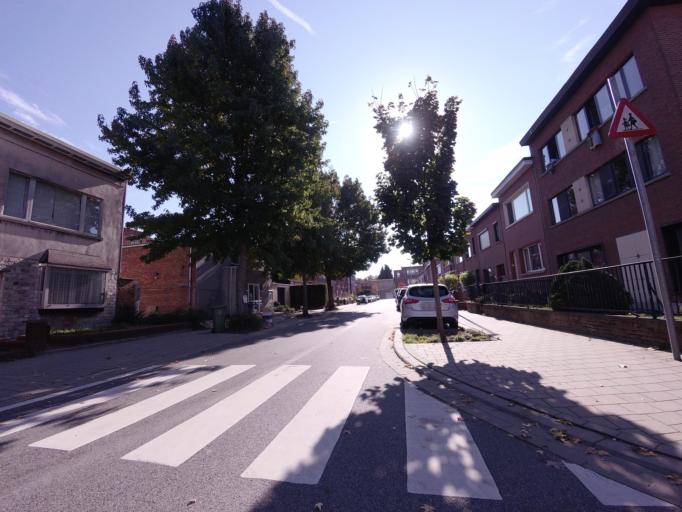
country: BE
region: Flanders
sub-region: Provincie Antwerpen
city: Borsbeek
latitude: 51.2248
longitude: 4.4722
